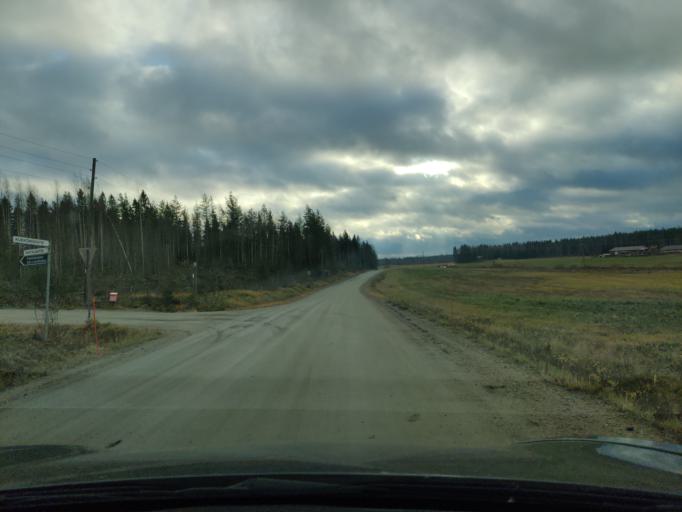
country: FI
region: Northern Savo
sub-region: Ylae-Savo
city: Kiuruvesi
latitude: 63.6380
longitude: 26.6351
